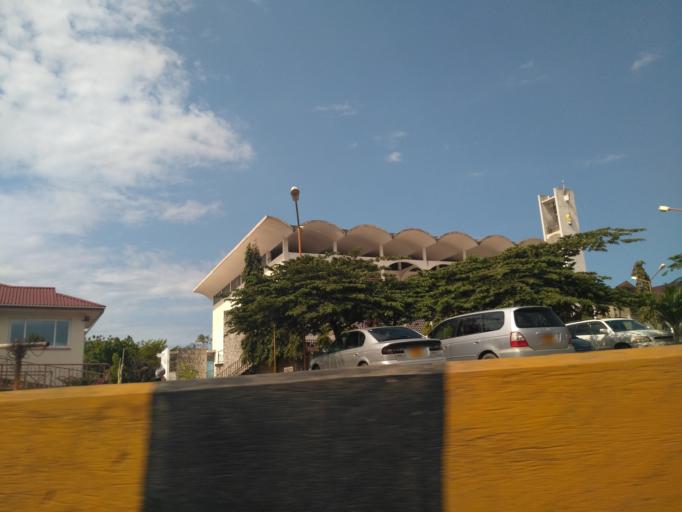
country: TZ
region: Dar es Salaam
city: Magomeni
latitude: -6.7801
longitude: 39.2750
